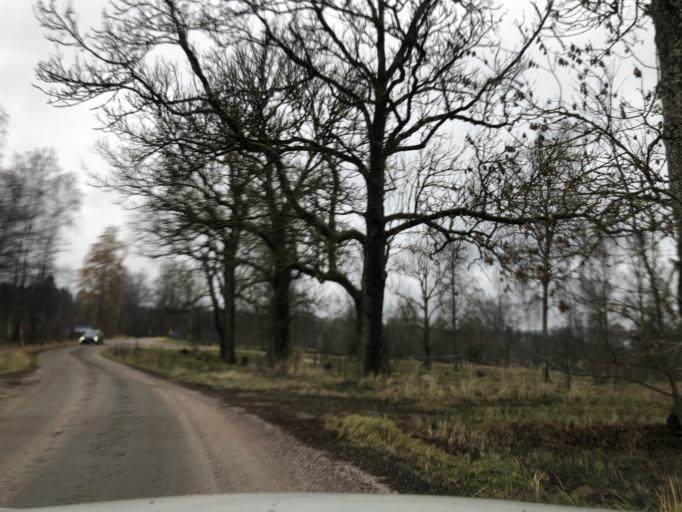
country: SE
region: Vaestra Goetaland
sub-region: Ulricehamns Kommun
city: Ulricehamn
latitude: 57.8518
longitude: 13.6341
